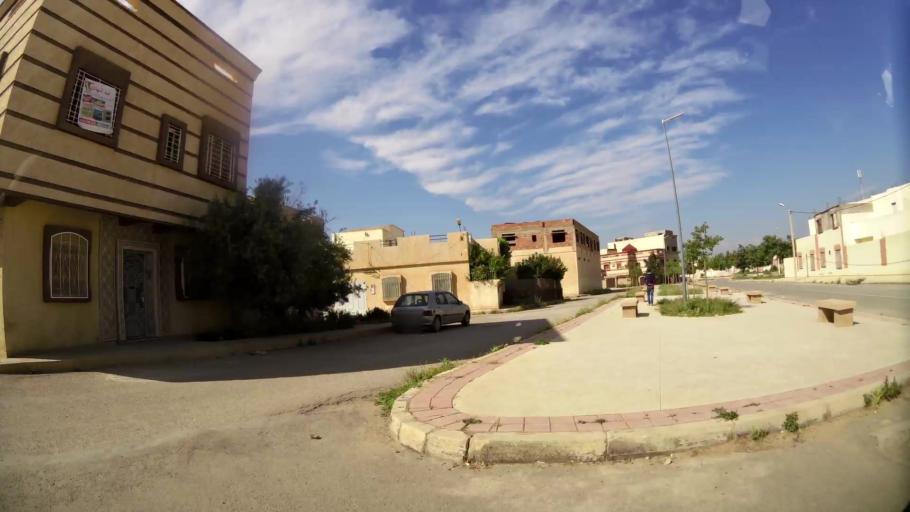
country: MA
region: Oriental
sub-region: Oujda-Angad
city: Oujda
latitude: 34.7094
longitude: -1.8832
